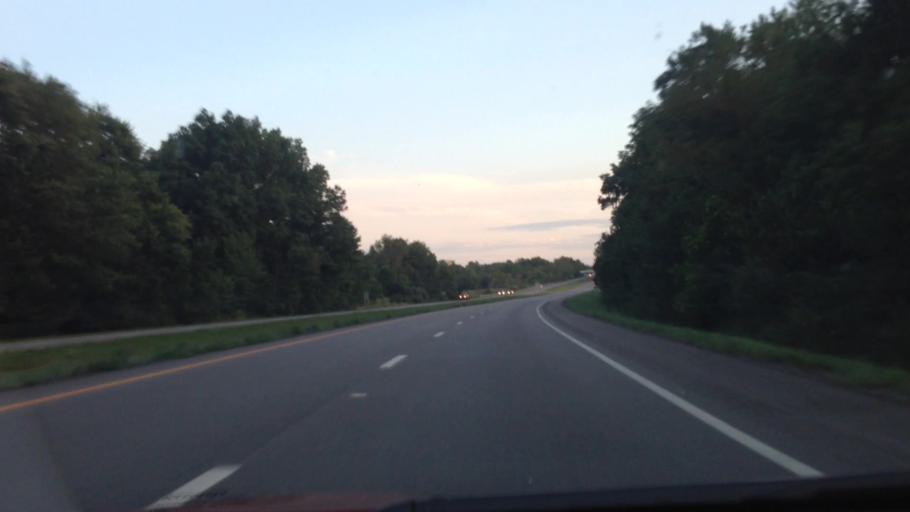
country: US
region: Ohio
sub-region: Summit County
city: Norton
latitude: 41.0651
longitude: -81.6625
